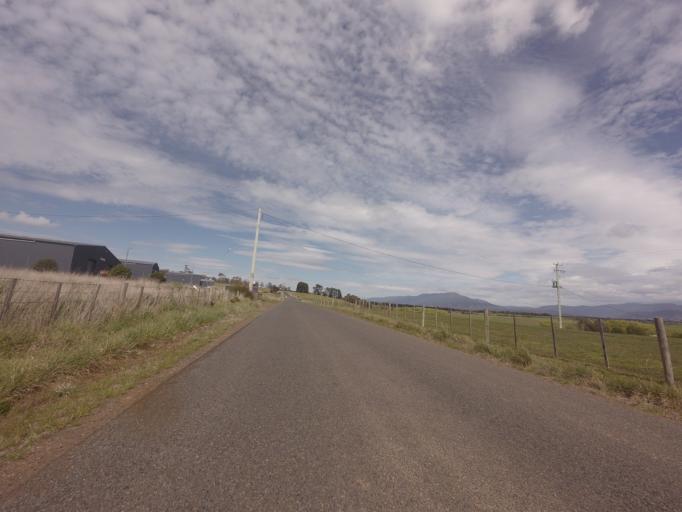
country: AU
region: Tasmania
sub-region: Northern Midlands
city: Longford
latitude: -41.7573
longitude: 147.2070
